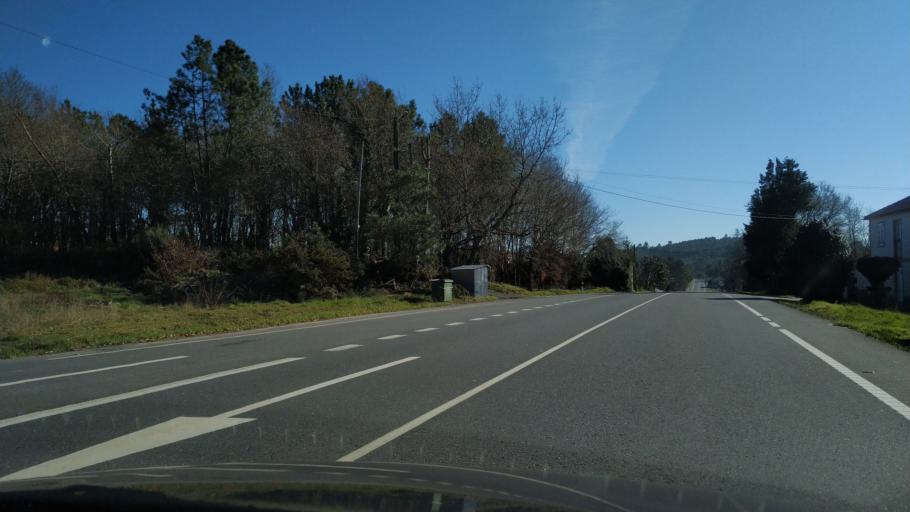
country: ES
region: Galicia
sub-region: Provincia da Coruna
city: Ribeira
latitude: 42.7567
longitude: -8.3642
